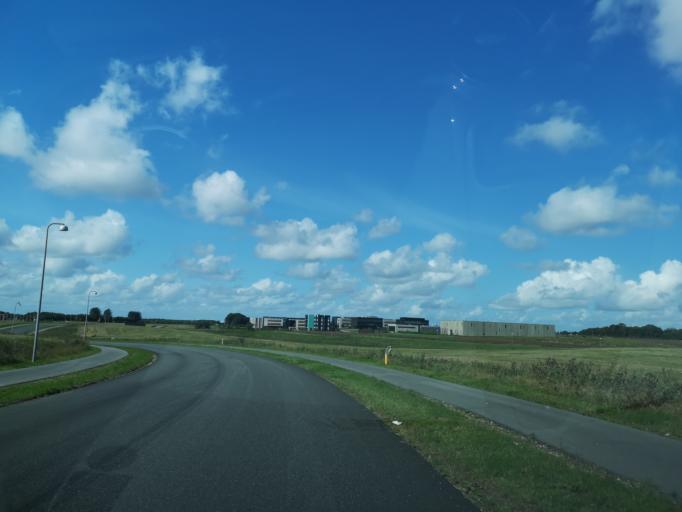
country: DK
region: Central Jutland
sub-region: Holstebro Kommune
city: Holstebro
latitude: 56.3911
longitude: 8.6208
